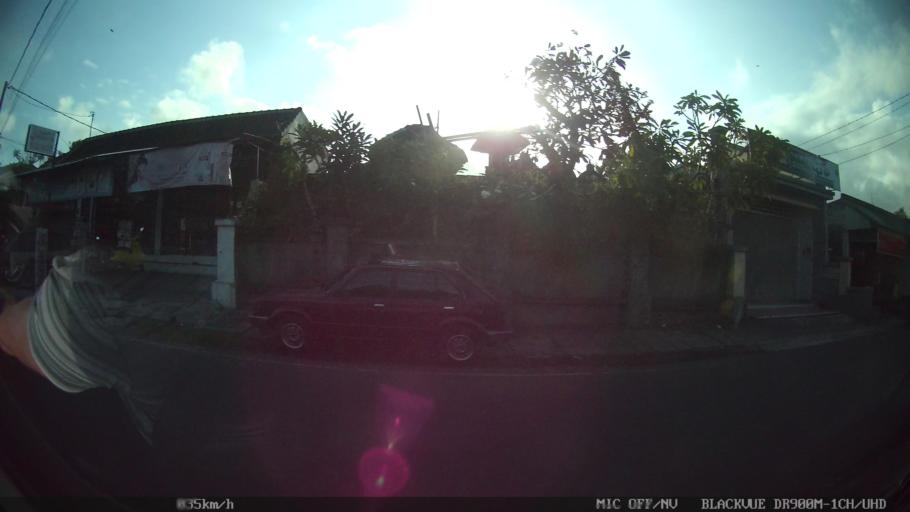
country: ID
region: Bali
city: Banjar Batur
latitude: -8.6049
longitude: 115.2137
